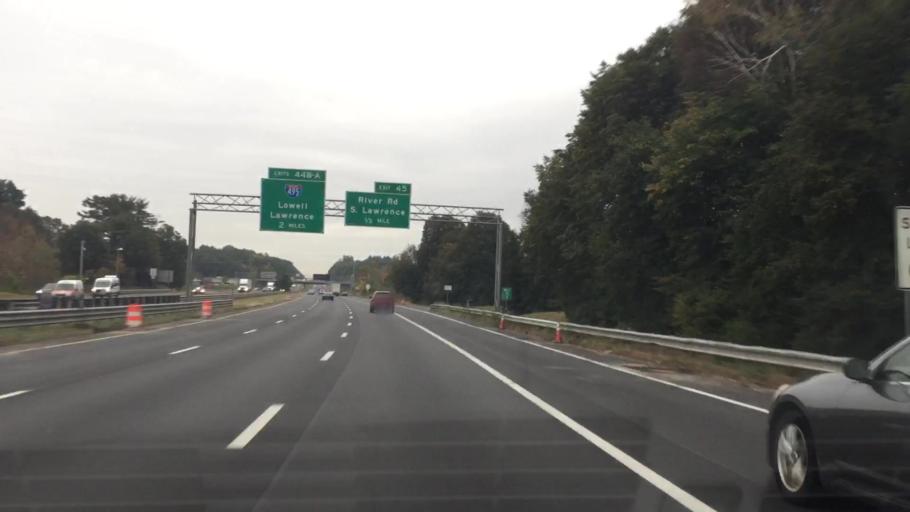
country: US
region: Massachusetts
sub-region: Essex County
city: Methuen
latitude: 42.6961
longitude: -71.2091
